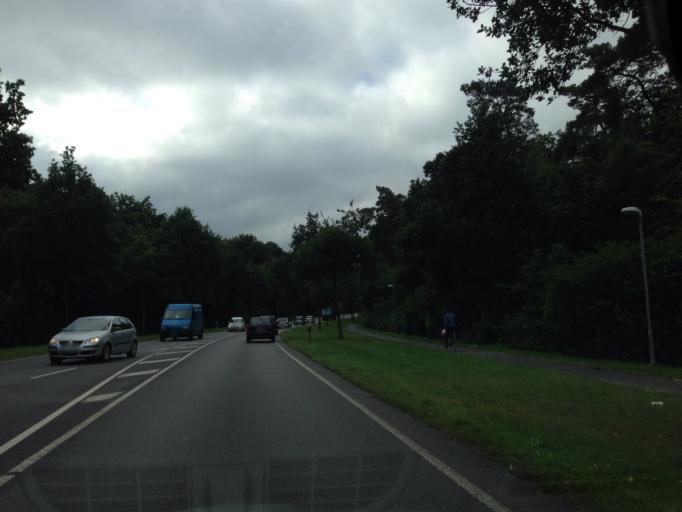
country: DE
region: Lower Saxony
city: Adendorf
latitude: 53.2666
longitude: 10.4284
